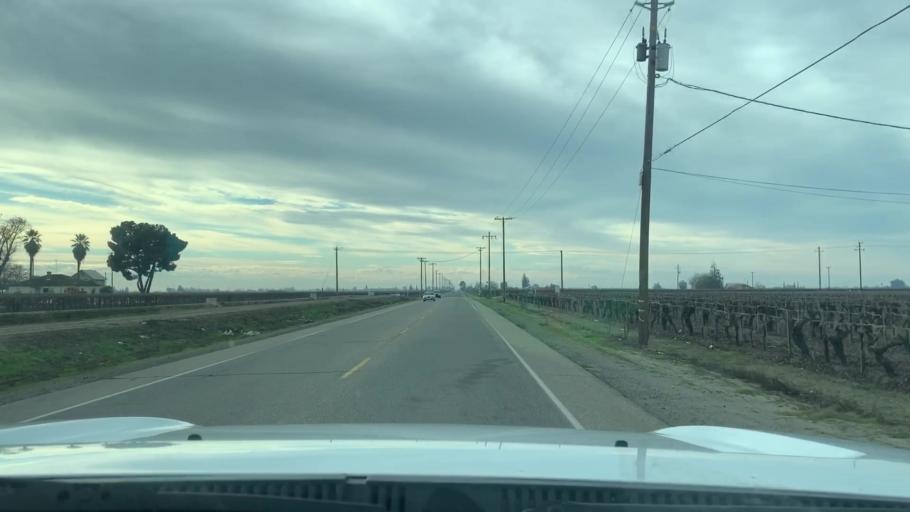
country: US
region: California
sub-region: Fresno County
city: Fowler
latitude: 36.6055
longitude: -119.7163
